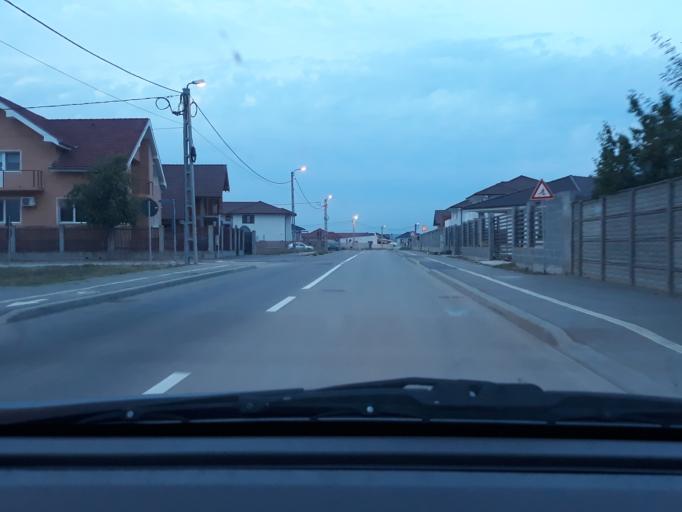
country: RO
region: Bihor
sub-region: Comuna Biharea
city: Oradea
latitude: 47.0272
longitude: 21.9253
